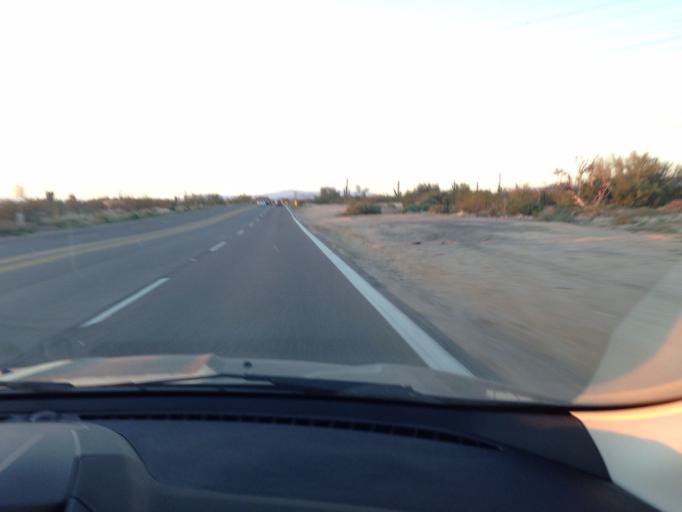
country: US
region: Arizona
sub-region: Maricopa County
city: Carefree
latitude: 33.7087
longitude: -111.9719
